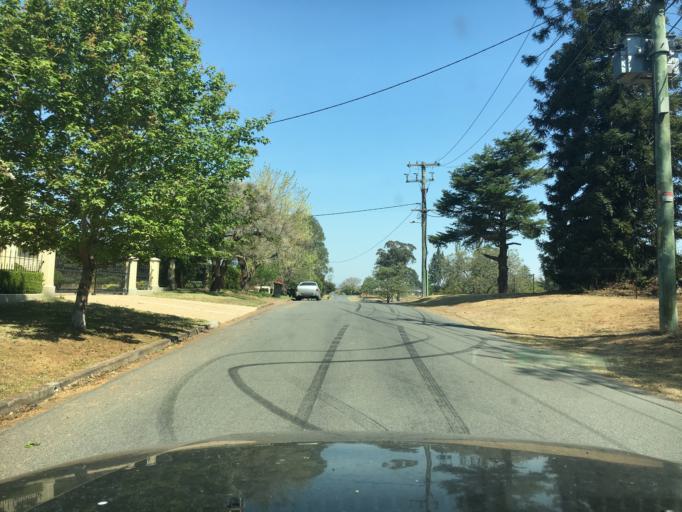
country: AU
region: New South Wales
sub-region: Singleton
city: Singleton
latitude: -32.5667
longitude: 151.1874
